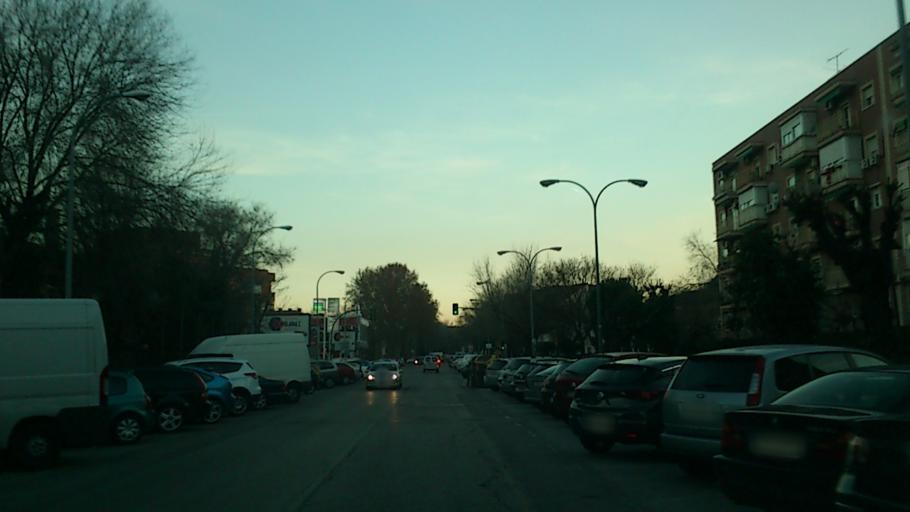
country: ES
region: Madrid
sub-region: Provincia de Madrid
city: San Fernando de Henares
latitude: 40.4314
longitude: -3.5388
